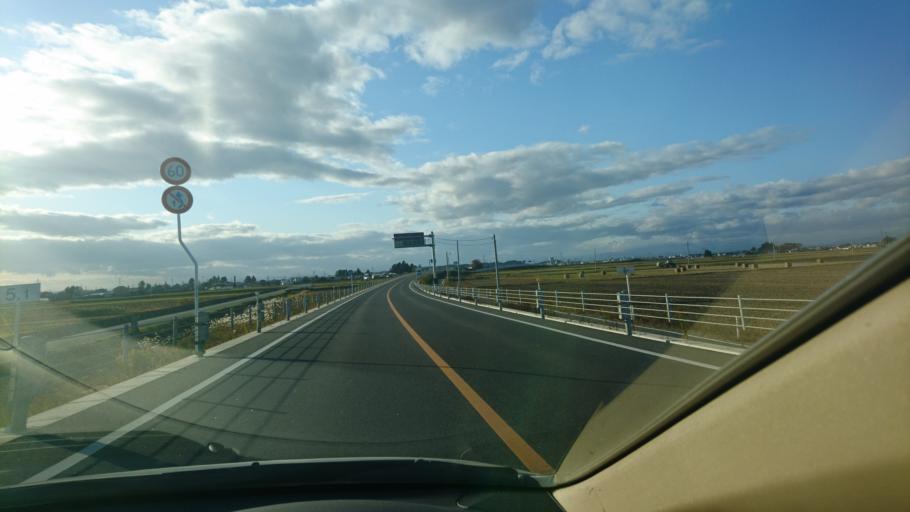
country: JP
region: Miyagi
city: Wakuya
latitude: 38.6865
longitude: 141.2295
